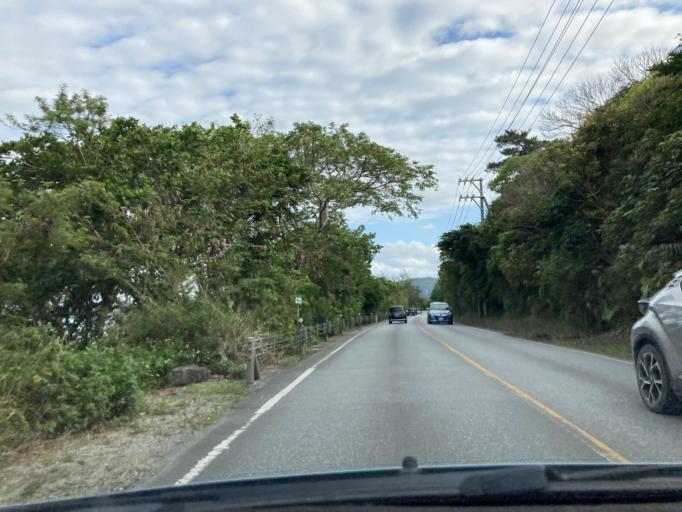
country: JP
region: Okinawa
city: Nago
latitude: 26.6429
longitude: 127.9987
